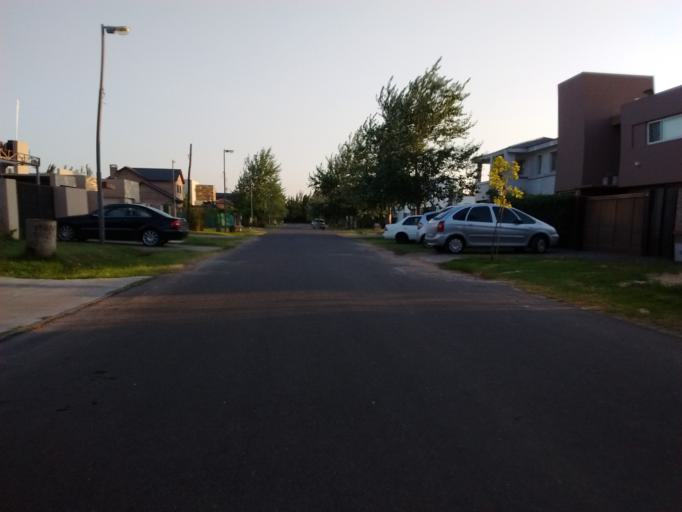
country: AR
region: Santa Fe
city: Funes
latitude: -32.9171
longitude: -60.7727
